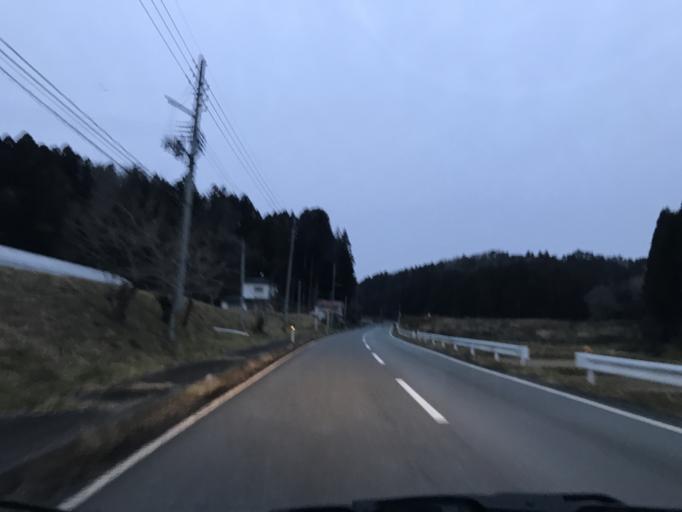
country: JP
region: Iwate
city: Ichinoseki
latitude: 38.8152
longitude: 141.1159
